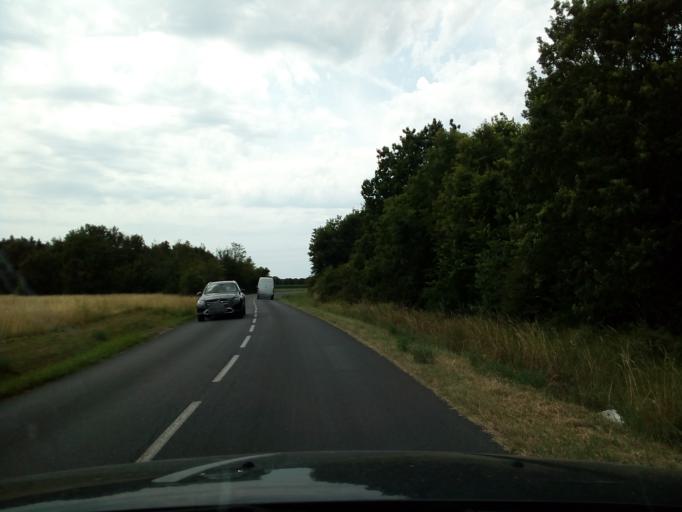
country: FR
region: Poitou-Charentes
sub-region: Departement de la Charente-Maritime
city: Dolus-d'Oleron
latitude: 45.9365
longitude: -1.3113
